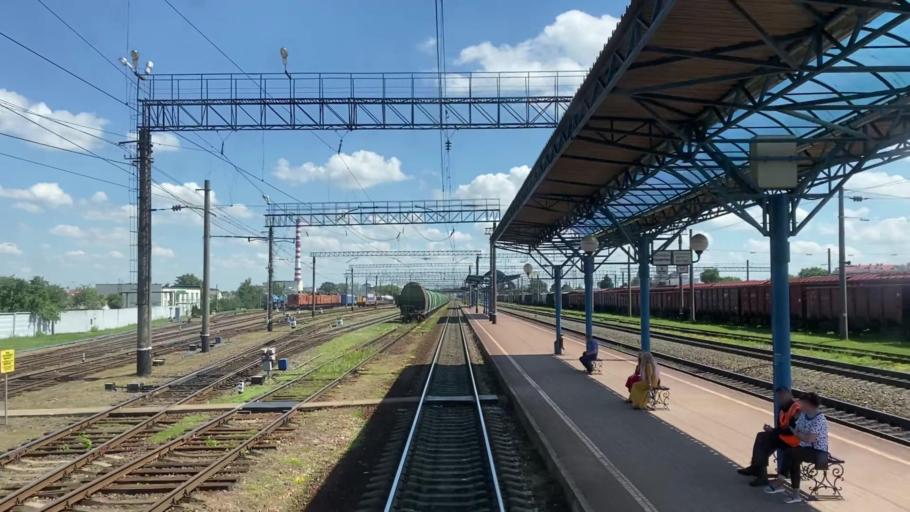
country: BY
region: Brest
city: Baranovichi
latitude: 53.1333
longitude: 25.9958
